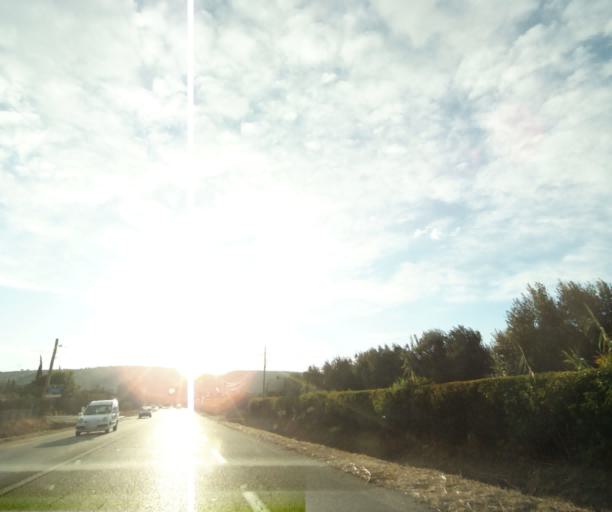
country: FR
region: Provence-Alpes-Cote d'Azur
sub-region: Departement des Bouches-du-Rhone
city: Chateauneuf-les-Martigues
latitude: 43.3796
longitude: 5.1898
